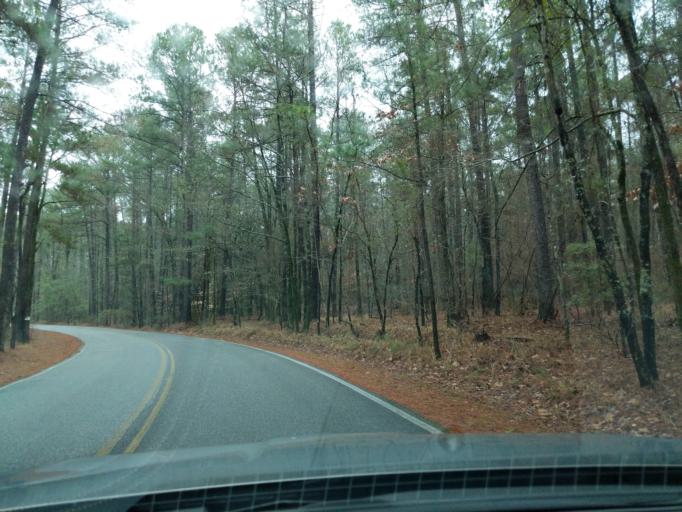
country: US
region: Georgia
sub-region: Columbia County
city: Appling
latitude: 33.6445
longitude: -82.3876
